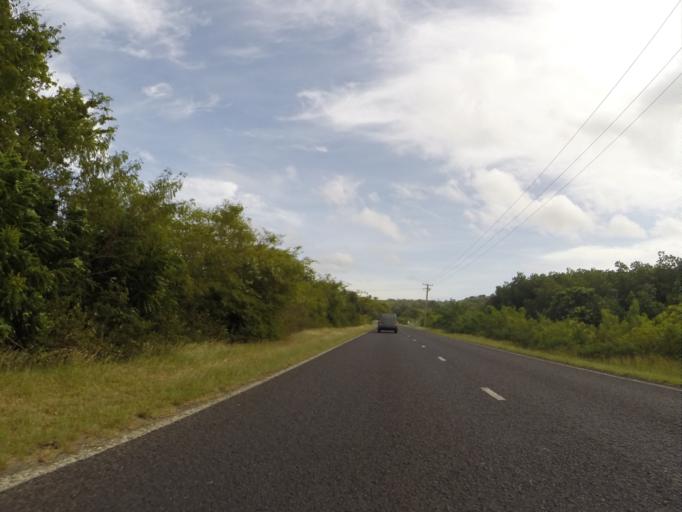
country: FJ
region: Western
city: Nadi
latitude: -18.1533
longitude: 177.4451
